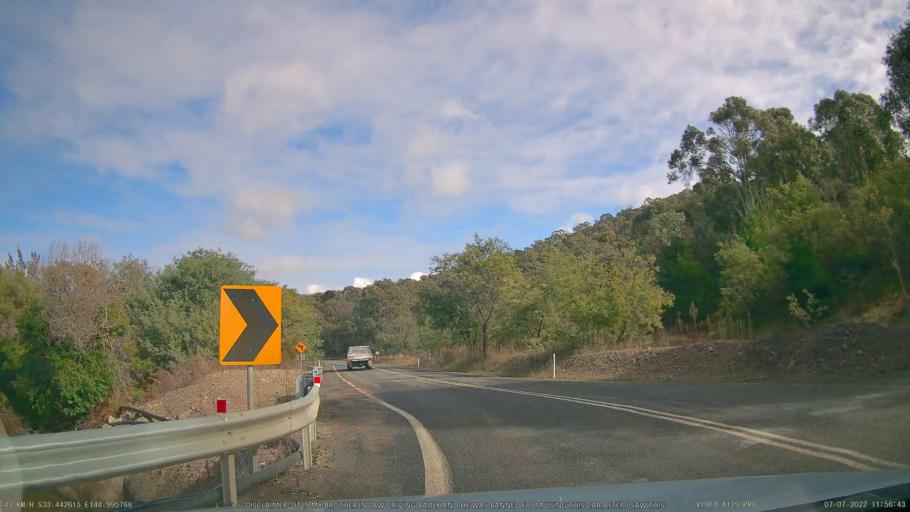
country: AU
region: New South Wales
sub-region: Blayney
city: Millthorpe
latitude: -33.4426
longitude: 148.9954
